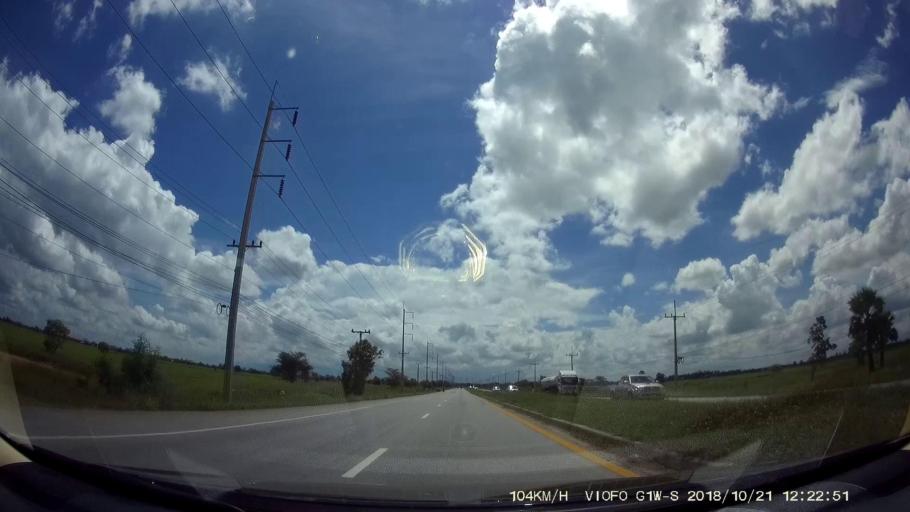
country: TH
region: Nakhon Ratchasima
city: Dan Khun Thot
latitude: 15.2549
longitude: 101.7892
